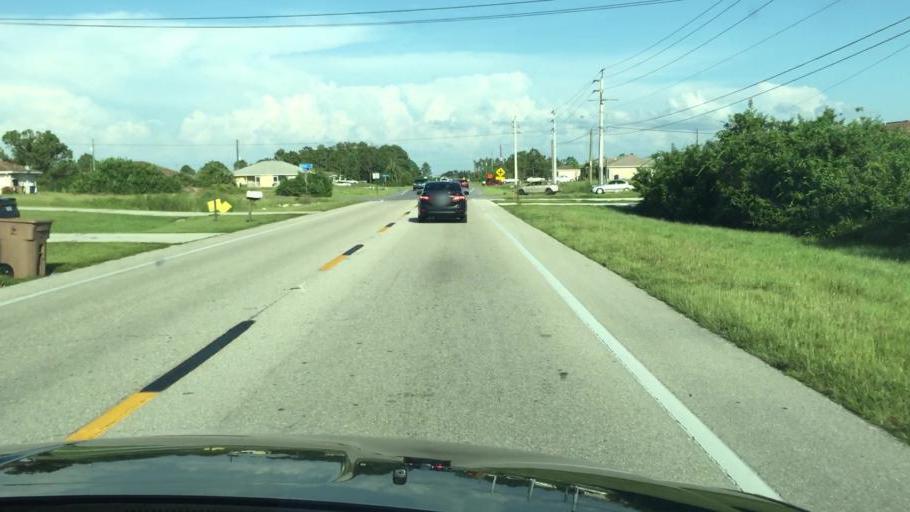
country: US
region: Florida
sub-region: Lee County
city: Gateway
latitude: 26.5940
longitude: -81.7224
